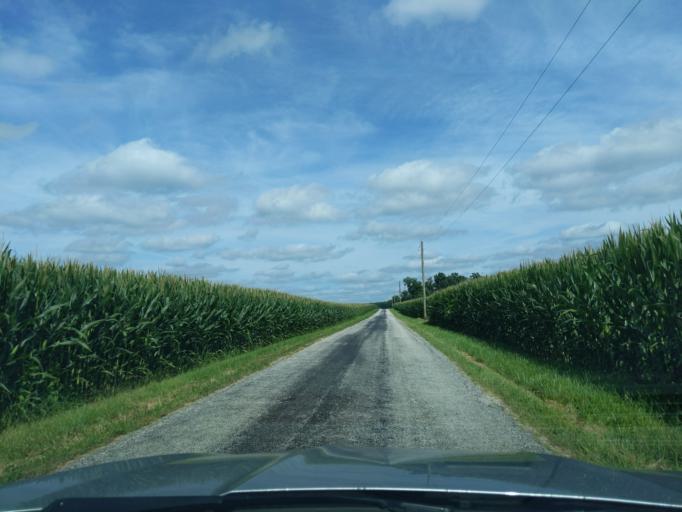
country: US
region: Indiana
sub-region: Ripley County
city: Osgood
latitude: 39.2352
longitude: -85.3745
